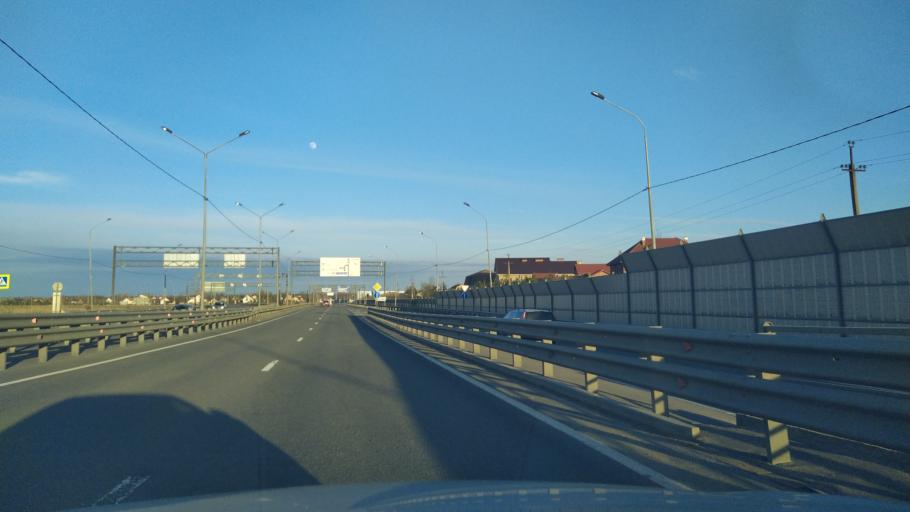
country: RU
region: St.-Petersburg
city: Aleksandrovskaya
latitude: 59.7424
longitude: 30.3157
